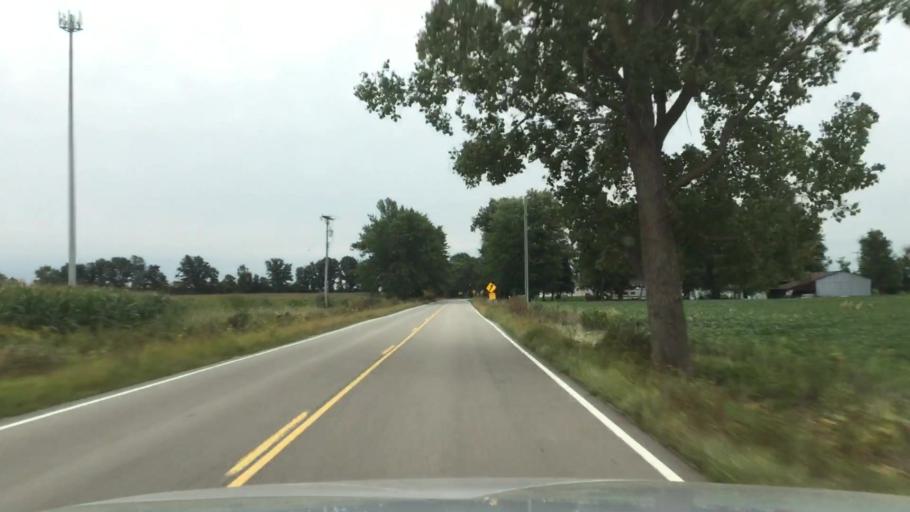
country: US
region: Michigan
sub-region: Washtenaw County
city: Milan
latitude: 42.0871
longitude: -83.7351
